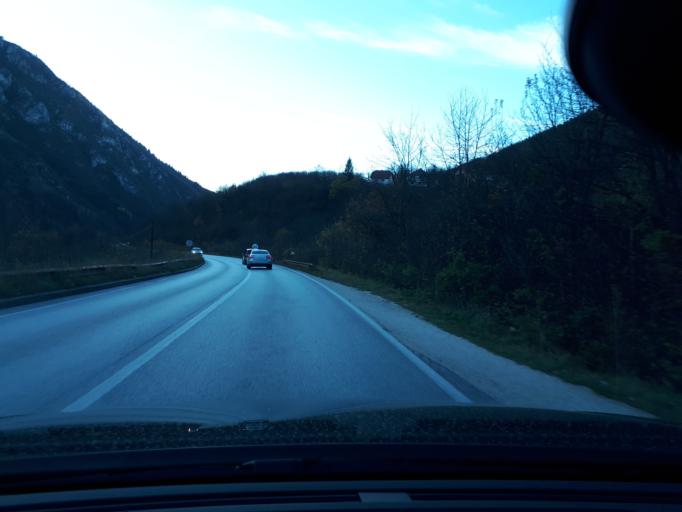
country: BA
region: Republika Srpska
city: Pale
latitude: 43.8413
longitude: 18.4840
